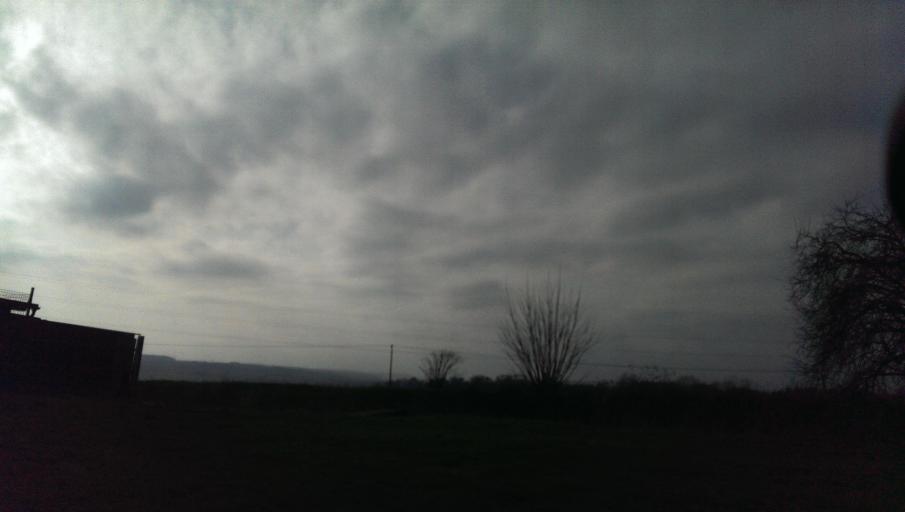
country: CZ
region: Zlin
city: Tlumacov
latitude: 49.2496
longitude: 17.4936
